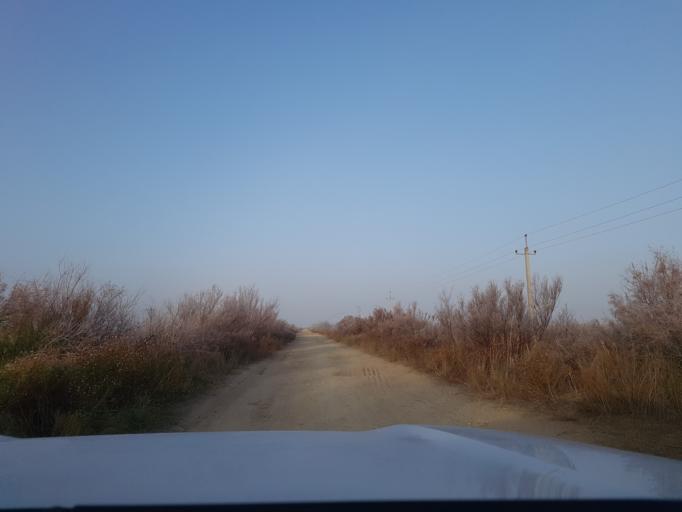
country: TM
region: Dasoguz
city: Koeneuergench
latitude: 41.8493
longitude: 58.3246
